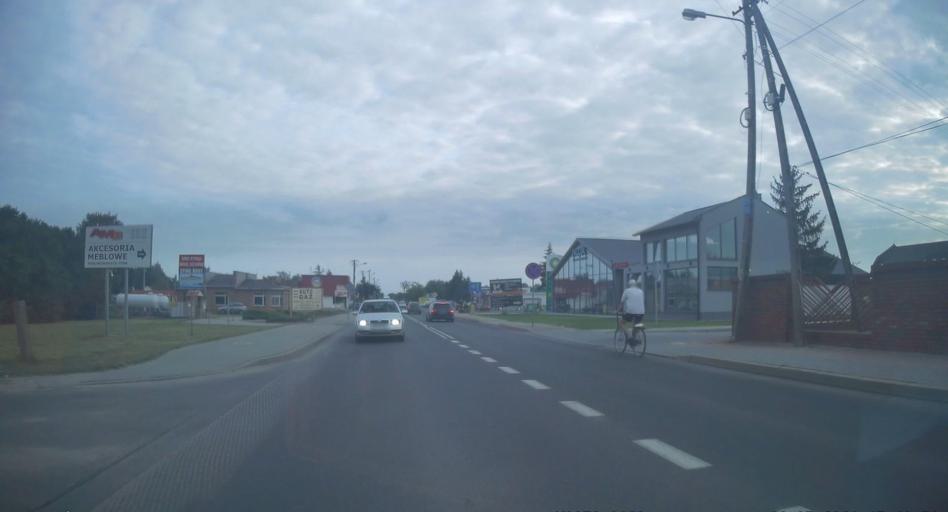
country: PL
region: Lodz Voivodeship
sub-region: Powiat radomszczanski
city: Radomsko
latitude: 51.0835
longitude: 19.4527
